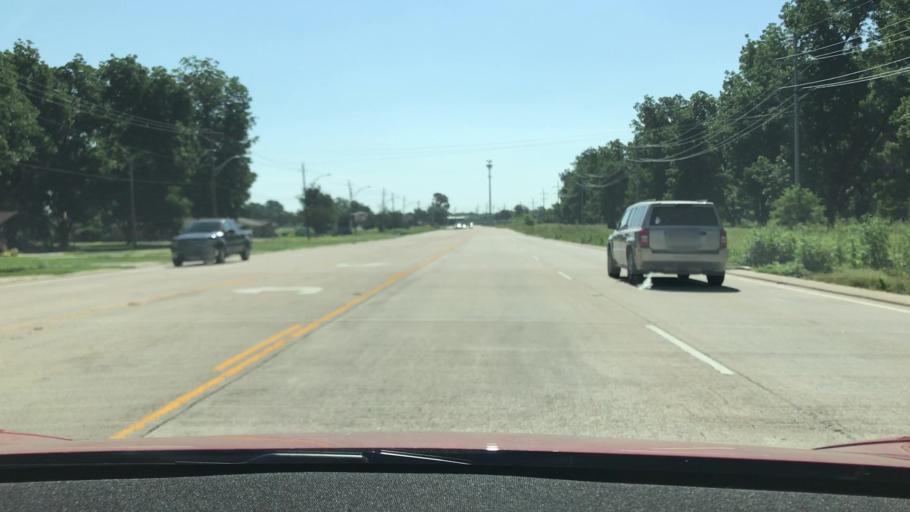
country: US
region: Louisiana
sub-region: Bossier Parish
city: Bossier City
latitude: 32.4008
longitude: -93.6998
